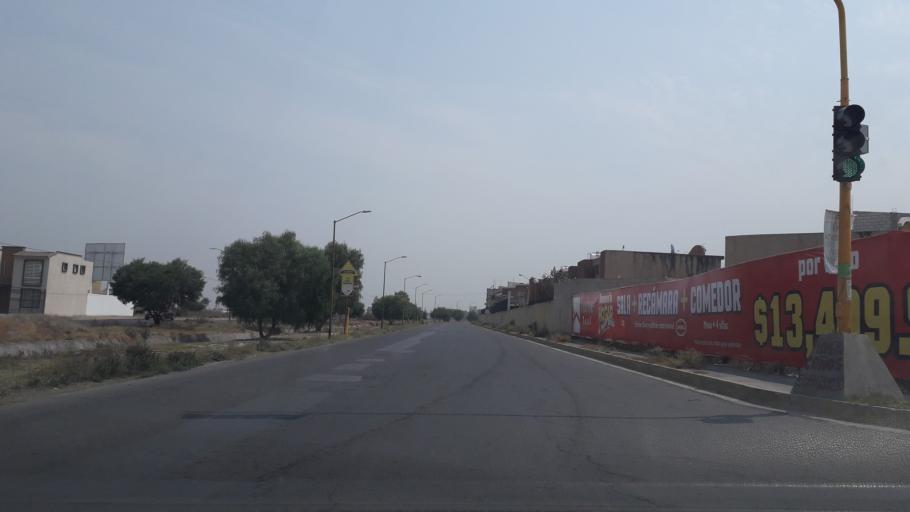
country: MX
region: Mexico
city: Santo Tomas Chiconautla
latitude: 19.6475
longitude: -99.0240
